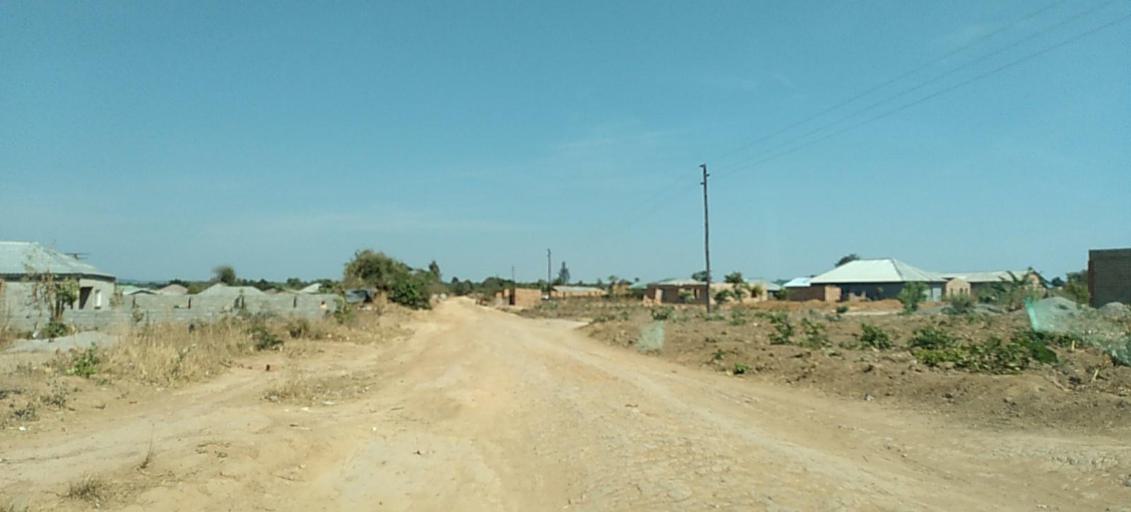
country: ZM
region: Copperbelt
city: Chililabombwe
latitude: -12.3366
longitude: 27.8641
